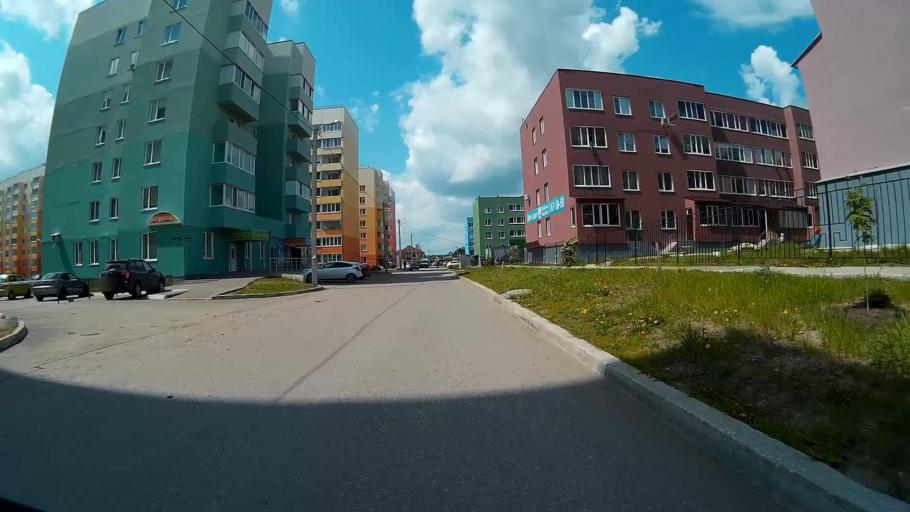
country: RU
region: Ulyanovsk
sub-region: Ulyanovskiy Rayon
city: Ulyanovsk
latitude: 54.3483
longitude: 48.3380
